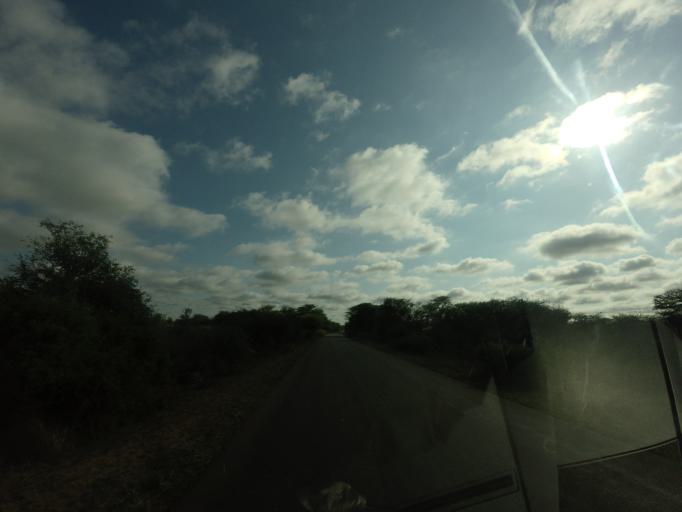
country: ZA
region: Mpumalanga
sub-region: Ehlanzeni District
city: Komatipoort
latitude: -25.2118
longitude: 31.8702
